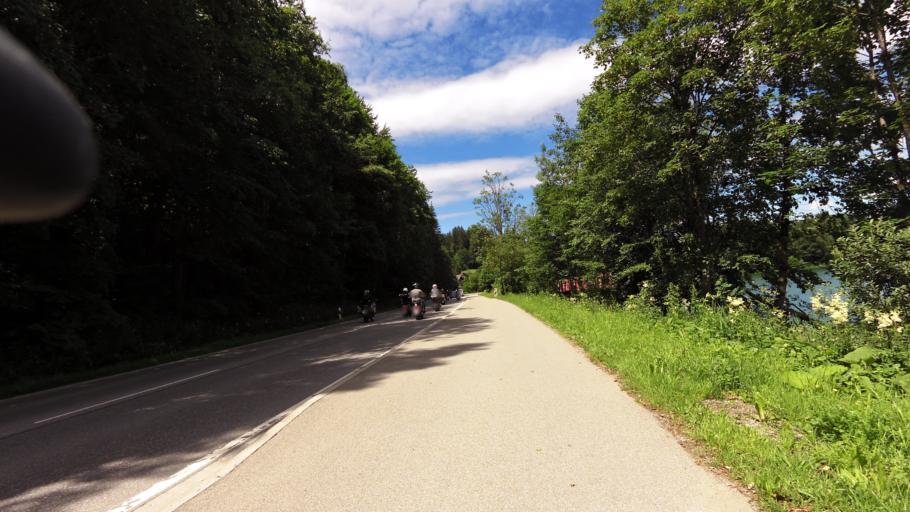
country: DE
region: Bavaria
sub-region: Upper Bavaria
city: Bad Wiessee
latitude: 47.6943
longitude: 11.7344
